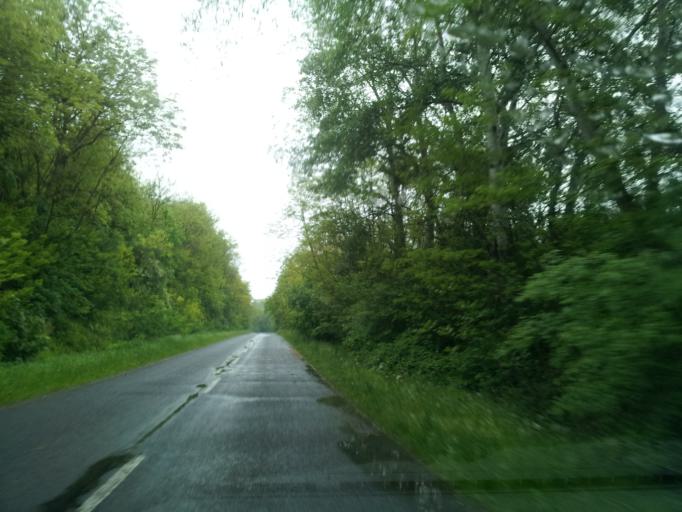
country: HU
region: Tolna
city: Bonyhad
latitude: 46.2599
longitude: 18.6085
